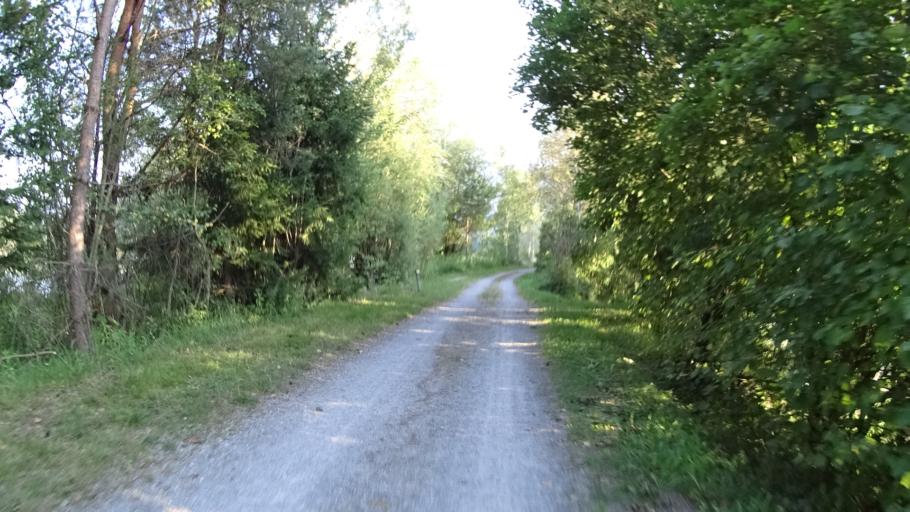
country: AT
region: Carinthia
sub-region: Politischer Bezirk Villach Land
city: Sankt Jakob
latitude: 46.5413
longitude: 14.0894
